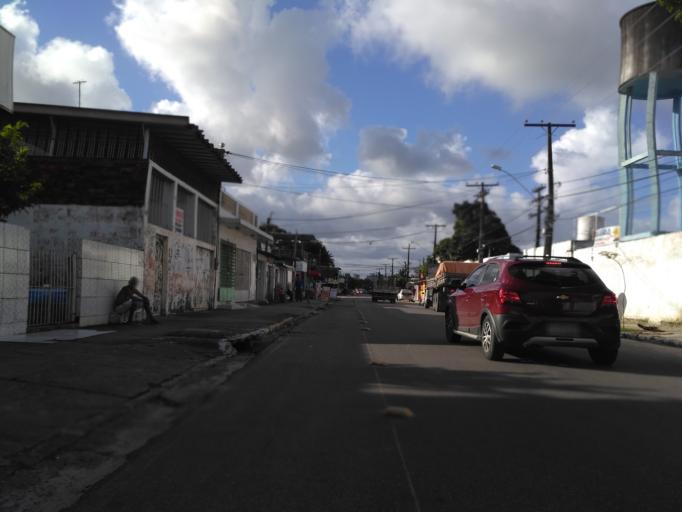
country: BR
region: Pernambuco
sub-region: Recife
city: Recife
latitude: -8.0591
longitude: -34.9423
